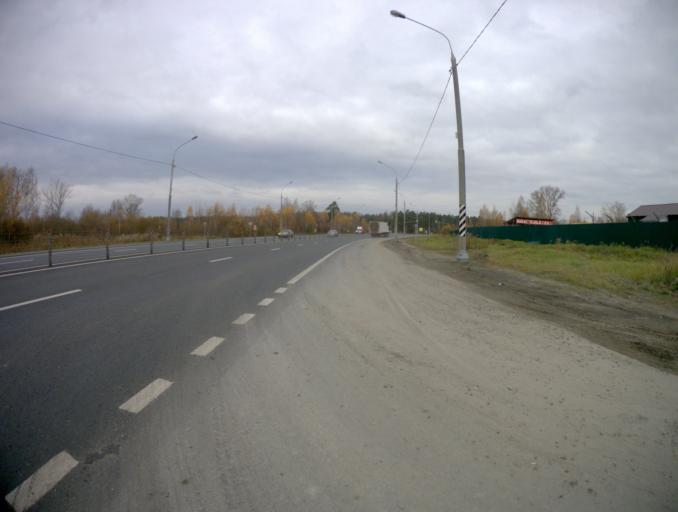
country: RU
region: Moskovskaya
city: Orekhovo-Zuyevo
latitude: 55.8418
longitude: 38.9674
